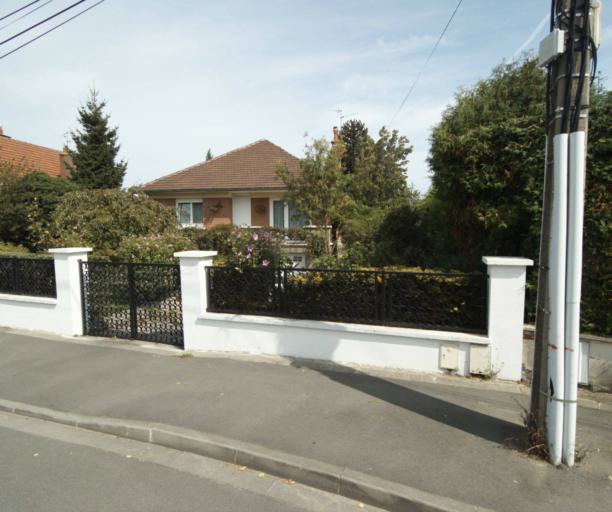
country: FR
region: Nord-Pas-de-Calais
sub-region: Departement du Nord
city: Faches-Thumesnil
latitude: 50.6064
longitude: 3.0603
